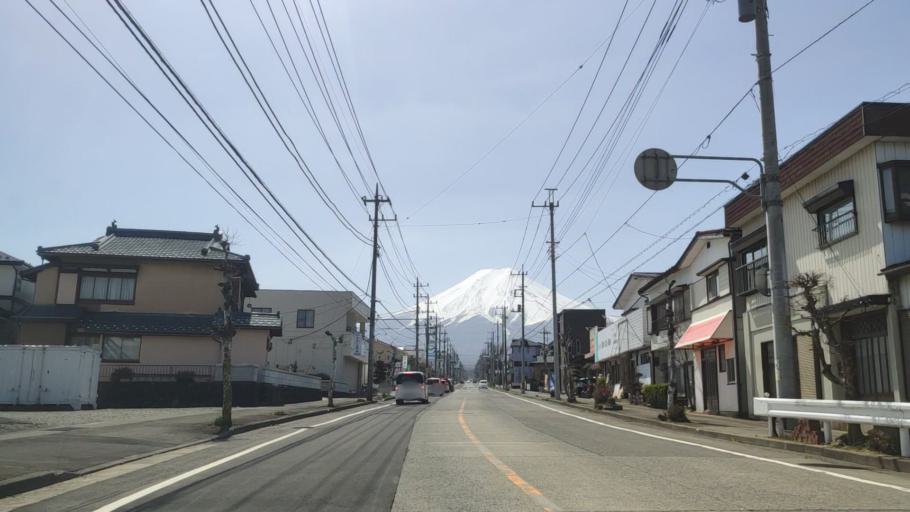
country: JP
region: Yamanashi
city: Fujikawaguchiko
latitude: 35.4911
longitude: 138.8090
